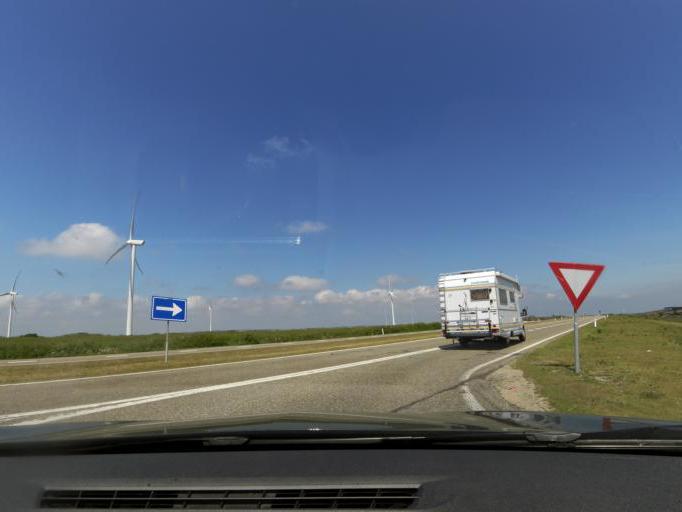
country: NL
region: Zeeland
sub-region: Schouwen-Duiveland
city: Burgh
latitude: 51.6343
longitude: 3.7034
